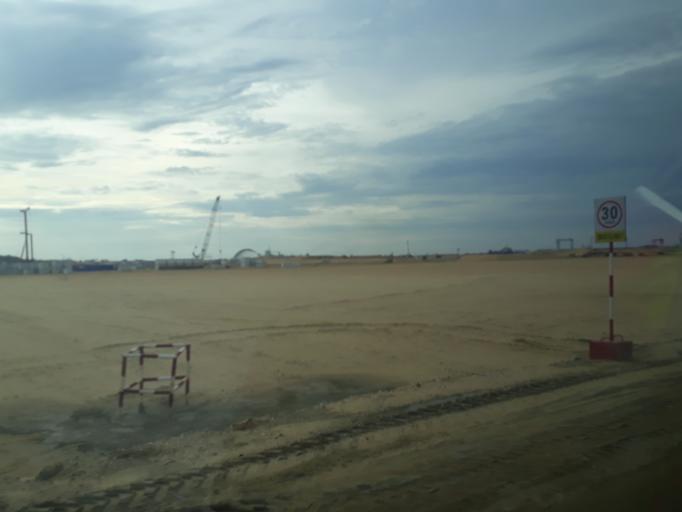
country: LK
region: Western
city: Colombo
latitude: 6.9312
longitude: 79.8392
